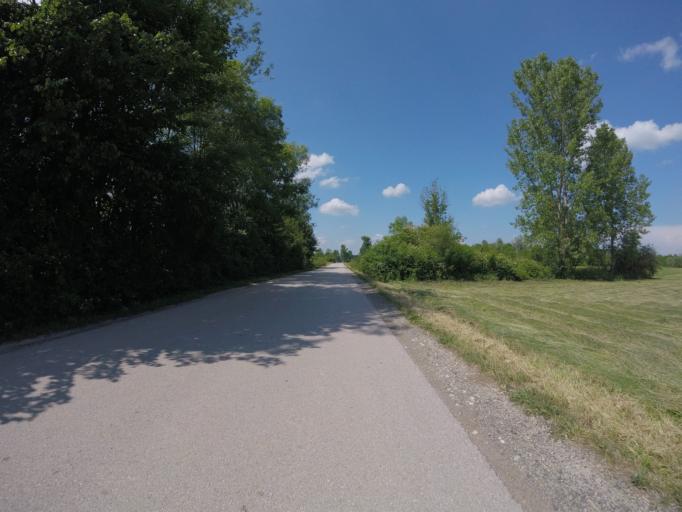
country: HR
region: Zagrebacka
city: Kuce
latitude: 45.6704
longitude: 16.1842
